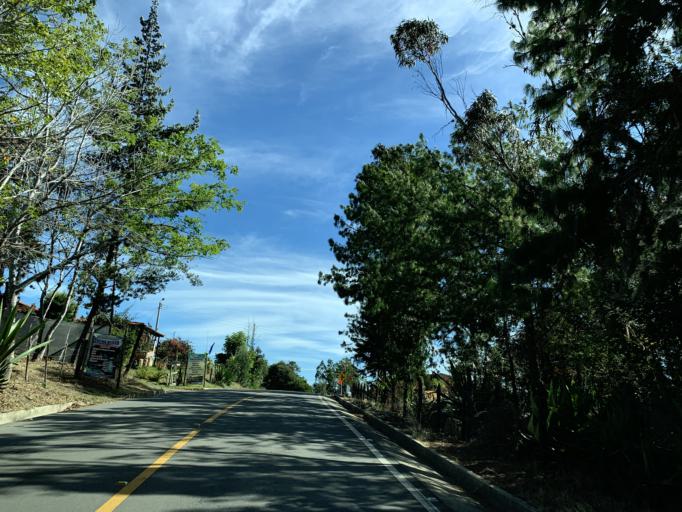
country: CO
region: Boyaca
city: Santa Sofia
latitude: 5.7020
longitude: -73.5904
